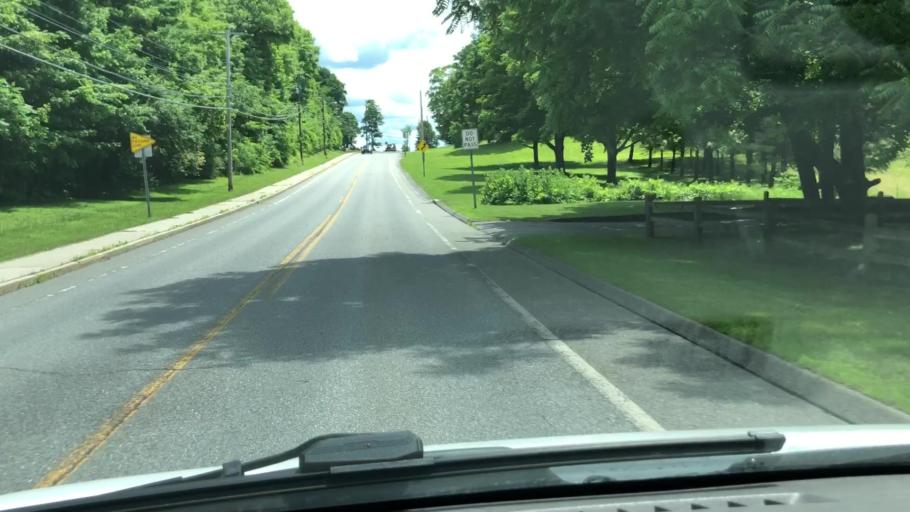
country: US
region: Massachusetts
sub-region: Berkshire County
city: Adams
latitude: 42.6034
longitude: -73.1177
